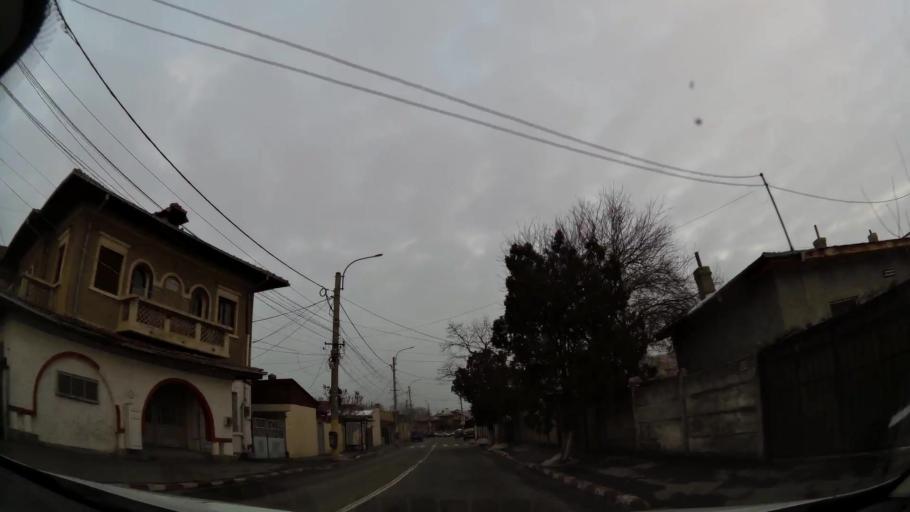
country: RO
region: Ilfov
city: Dobroesti
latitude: 44.4503
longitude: 26.1792
